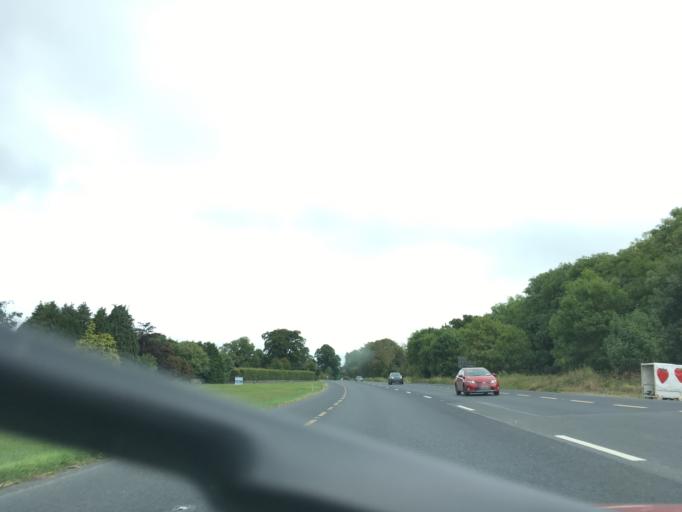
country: IE
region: Munster
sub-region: South Tipperary
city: Cluain Meala
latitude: 52.3655
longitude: -7.6235
